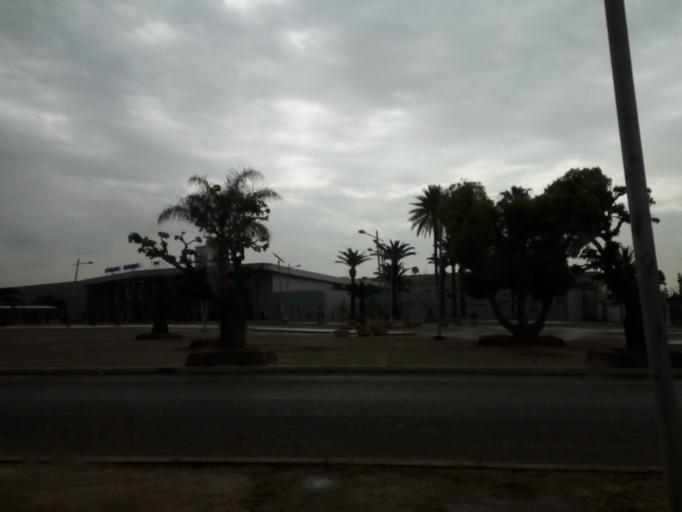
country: DZ
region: Alger
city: Dar el Beida
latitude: 36.7007
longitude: 3.2105
